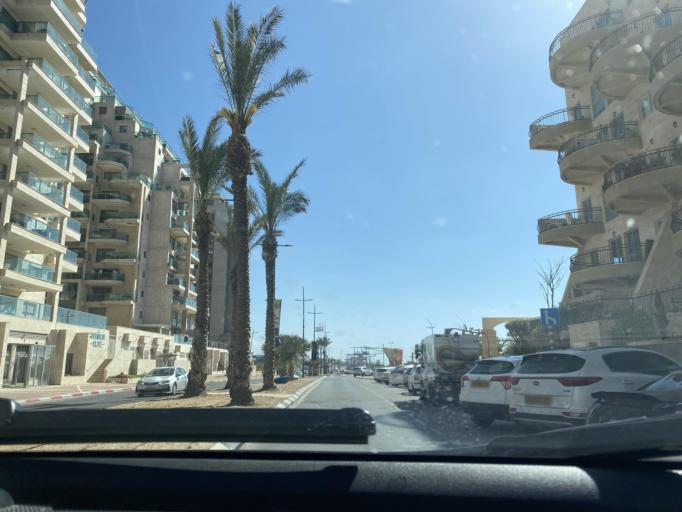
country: IL
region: Southern District
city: Ashqelon
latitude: 31.6791
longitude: 34.5571
